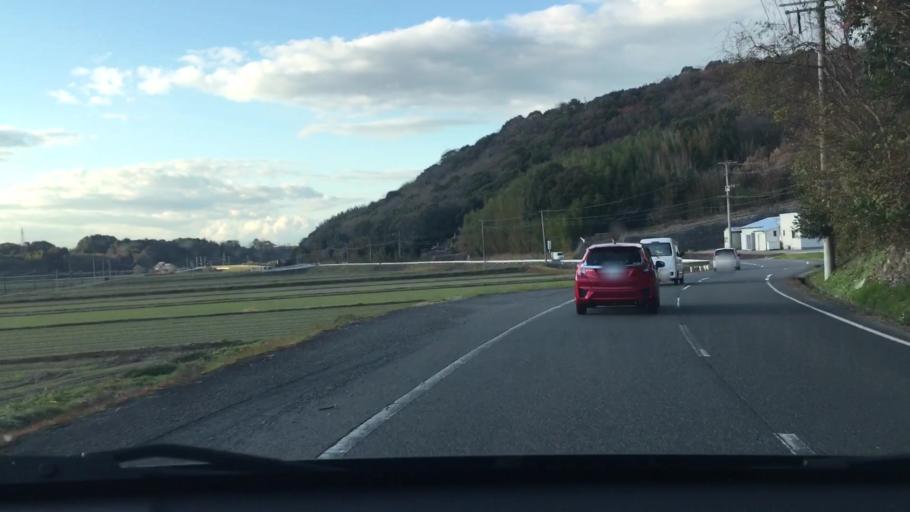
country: JP
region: Oita
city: Bungo-Takada-shi
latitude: 33.5088
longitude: 131.3590
